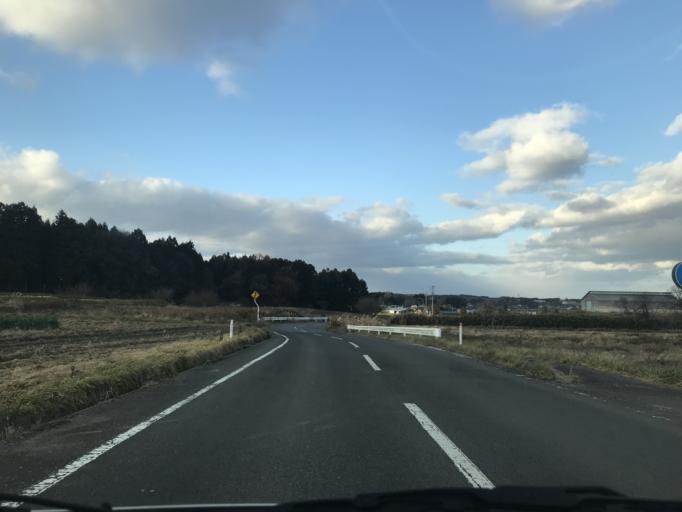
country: JP
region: Miyagi
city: Kogota
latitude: 38.6344
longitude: 141.0537
